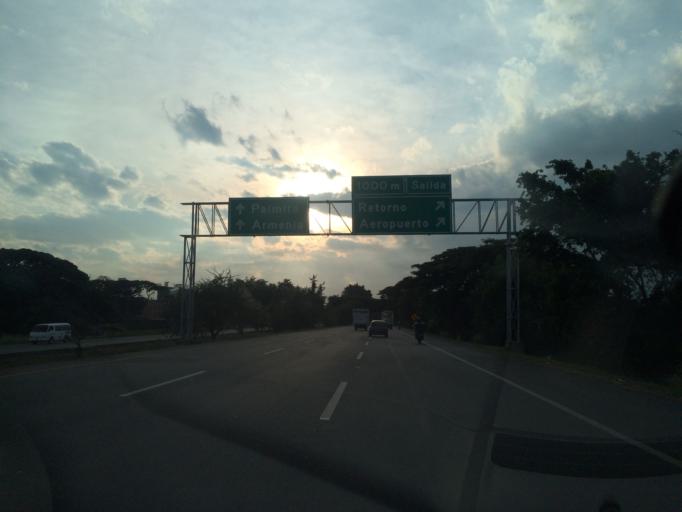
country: CO
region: Valle del Cauca
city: Palmira
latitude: 3.5087
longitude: -76.4069
